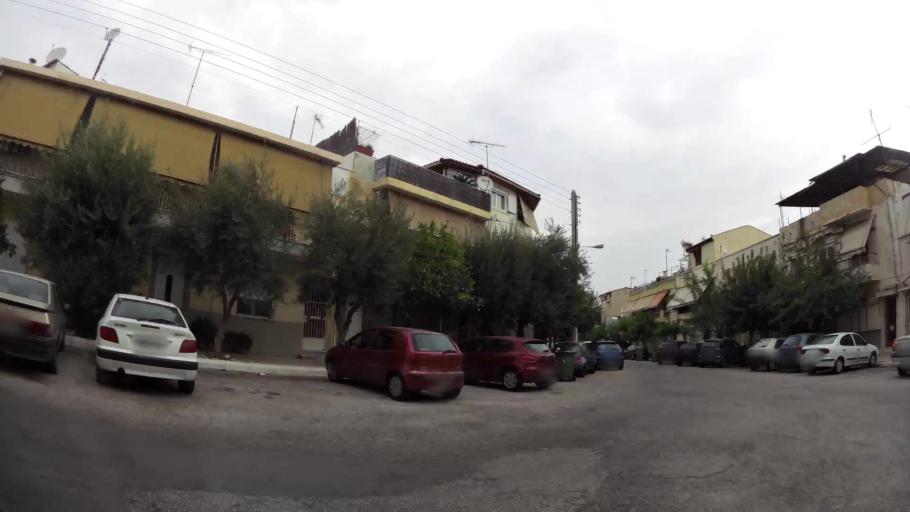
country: GR
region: Attica
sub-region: Nomos Piraios
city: Nikaia
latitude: 37.9595
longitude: 23.6511
